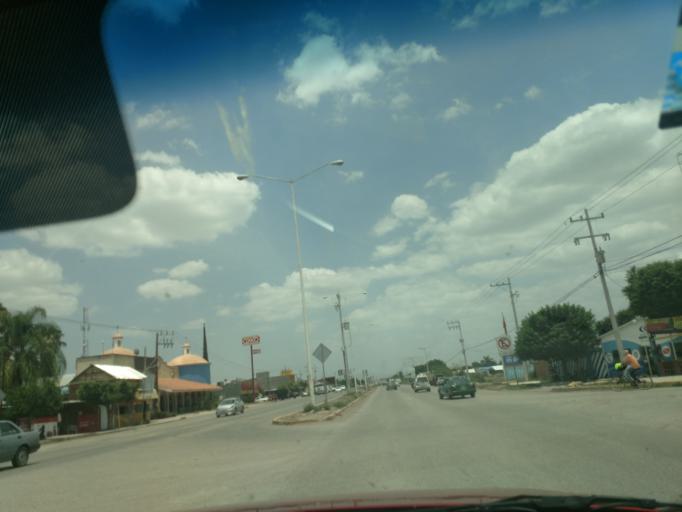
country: MX
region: San Luis Potosi
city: Ciudad Fernandez
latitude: 21.9369
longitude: -100.0298
